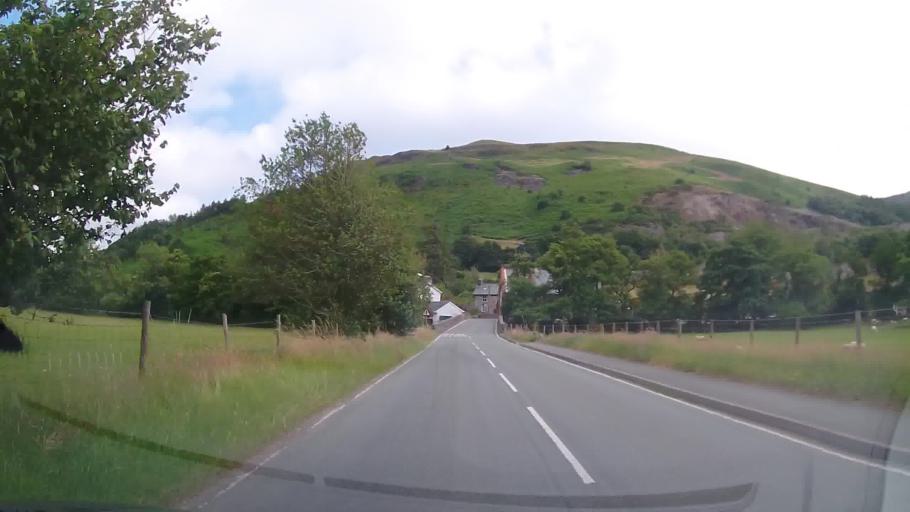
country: GB
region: Wales
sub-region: Sir Powys
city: Llangynog
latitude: 52.8234
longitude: -3.4054
